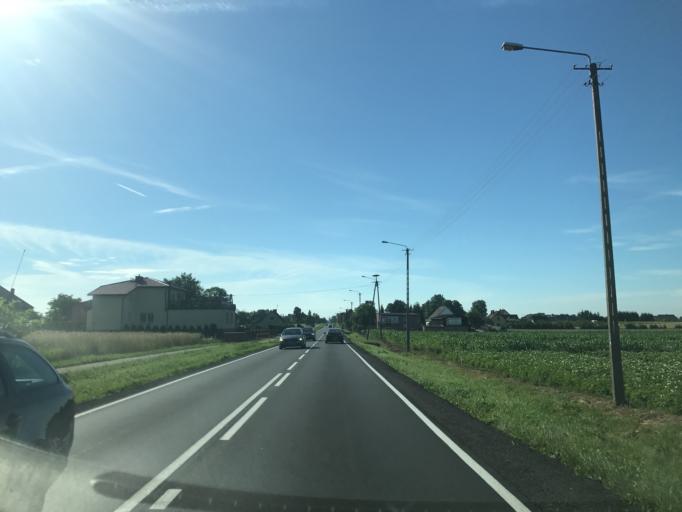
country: PL
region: Pomeranian Voivodeship
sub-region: Powiat czluchowski
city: Czluchow
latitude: 53.6831
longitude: 17.3338
